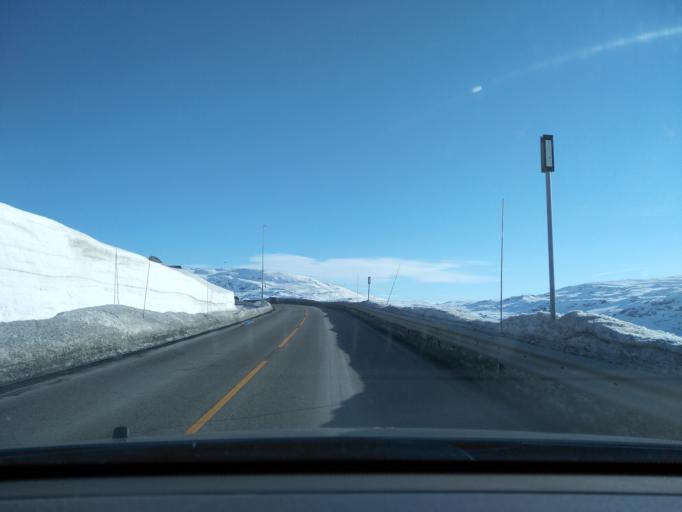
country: NO
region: Aust-Agder
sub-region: Bykle
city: Hovden
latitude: 59.8433
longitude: 6.9747
